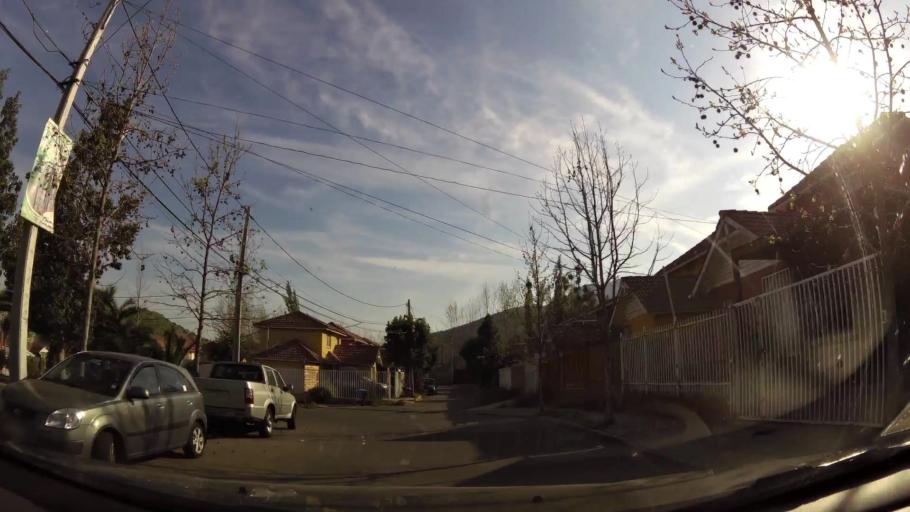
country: CL
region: Santiago Metropolitan
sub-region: Provincia de Cordillera
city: Puente Alto
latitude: -33.5593
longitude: -70.5428
